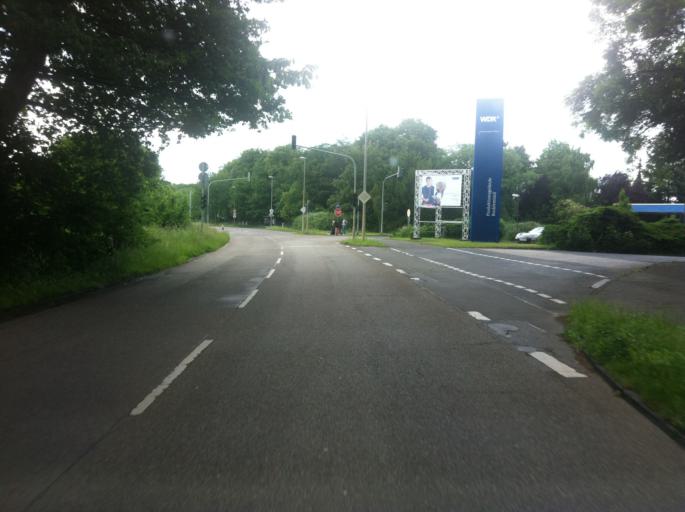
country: DE
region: North Rhine-Westphalia
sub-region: Regierungsbezirk Koln
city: Mengenich
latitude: 50.9707
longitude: 6.8649
